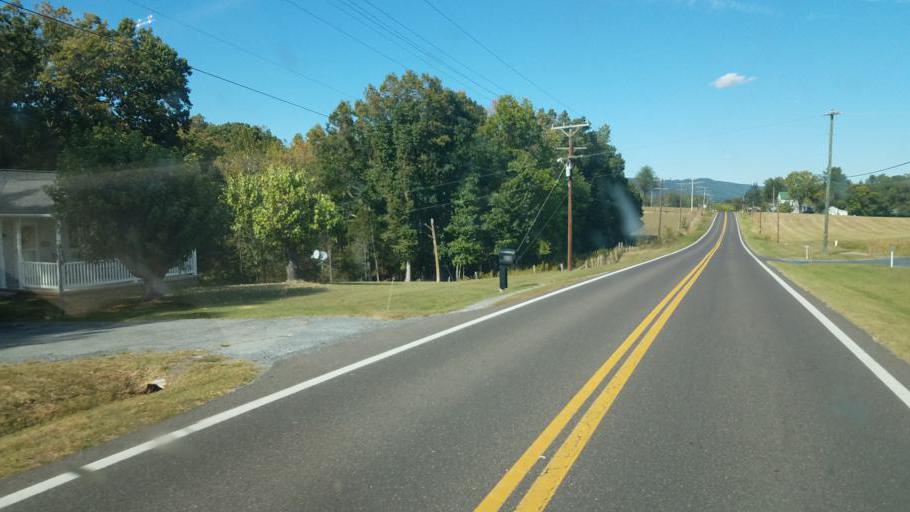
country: US
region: Virginia
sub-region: Page County
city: Luray
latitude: 38.7534
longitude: -78.4014
